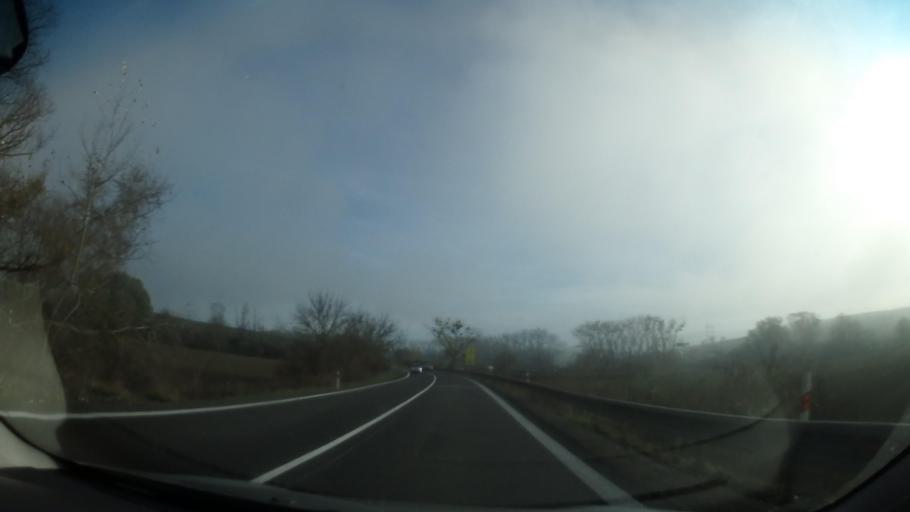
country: CZ
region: South Moravian
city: Zdanice
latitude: 49.0397
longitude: 17.0260
